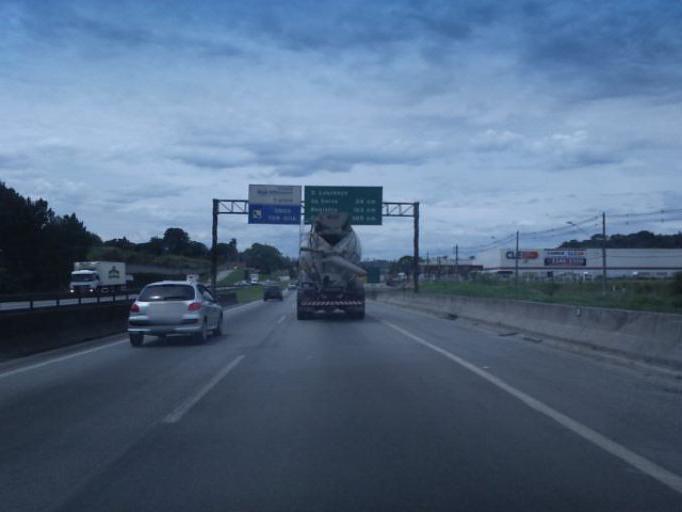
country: BR
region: Sao Paulo
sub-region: Embu
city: Embu
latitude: -23.6708
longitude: -46.8563
